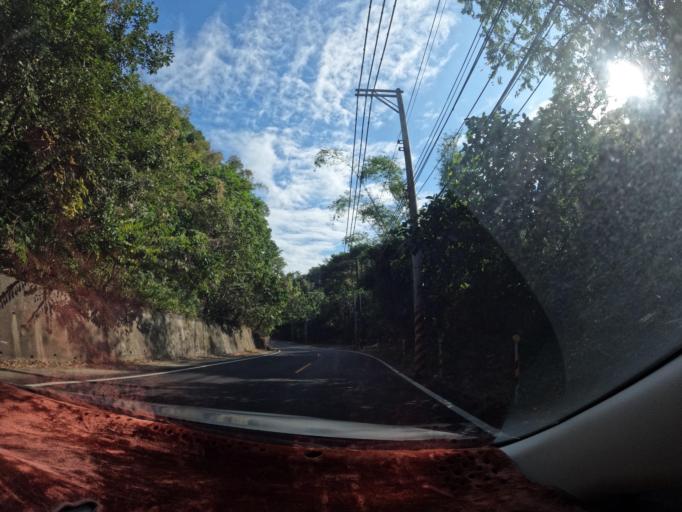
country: TW
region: Taiwan
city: Yujing
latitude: 23.0063
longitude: 120.3905
